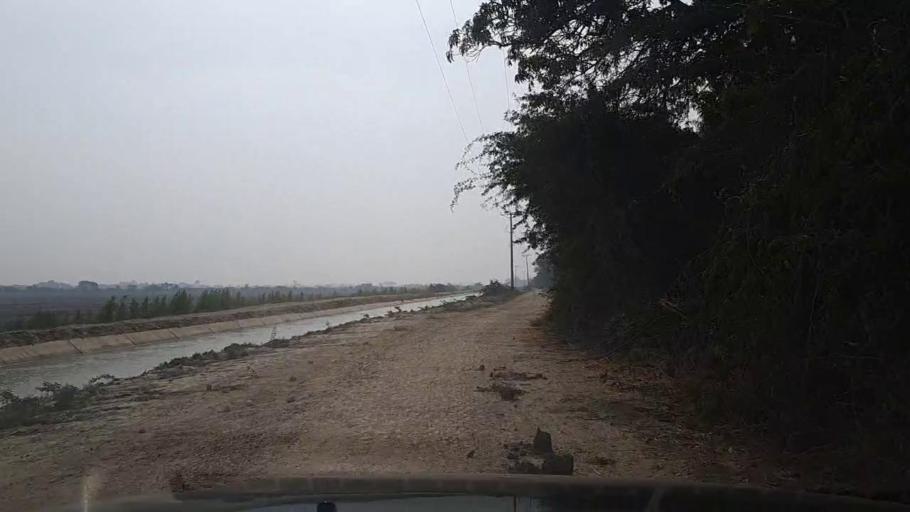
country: PK
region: Sindh
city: Mirpur Sakro
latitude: 24.5316
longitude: 67.8115
